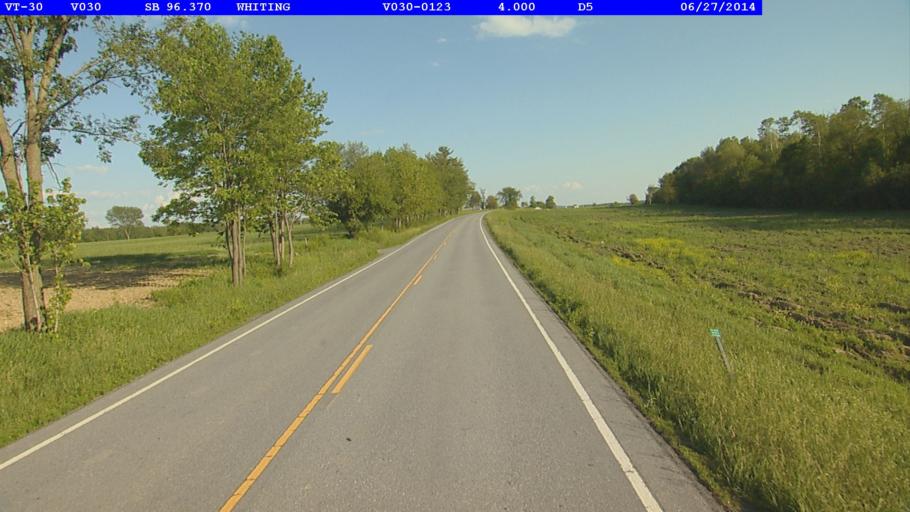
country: US
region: Vermont
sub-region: Addison County
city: Middlebury (village)
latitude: 43.8949
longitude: -73.2032
